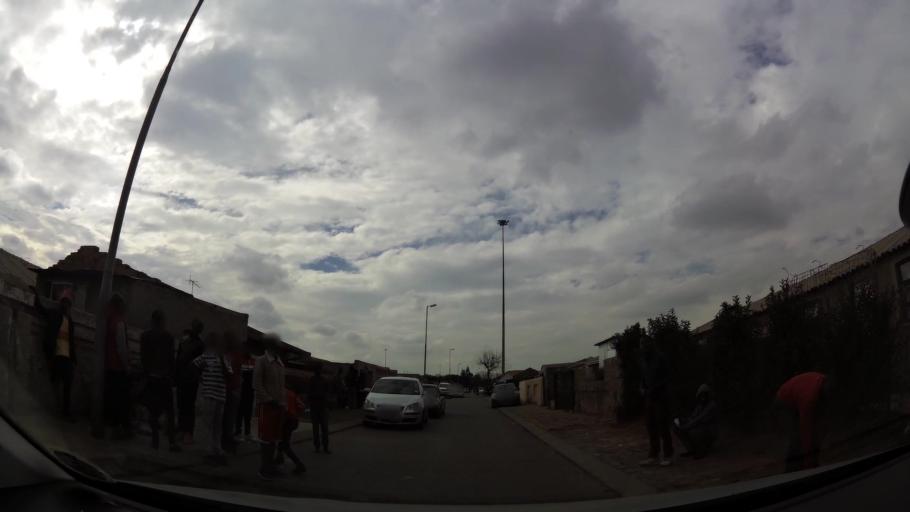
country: ZA
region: Gauteng
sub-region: City of Johannesburg Metropolitan Municipality
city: Soweto
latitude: -26.2737
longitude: 27.8534
